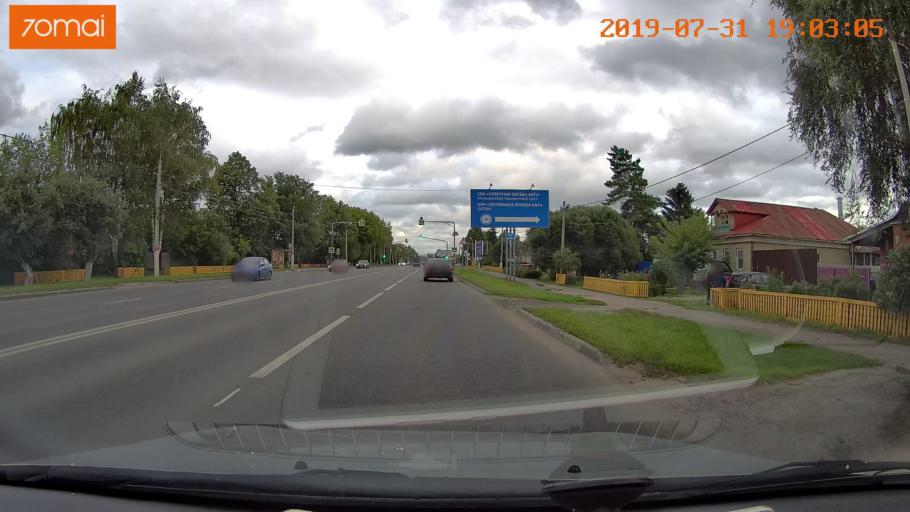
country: RU
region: Moskovskaya
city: Raduzhnyy
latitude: 55.1168
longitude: 38.7361
